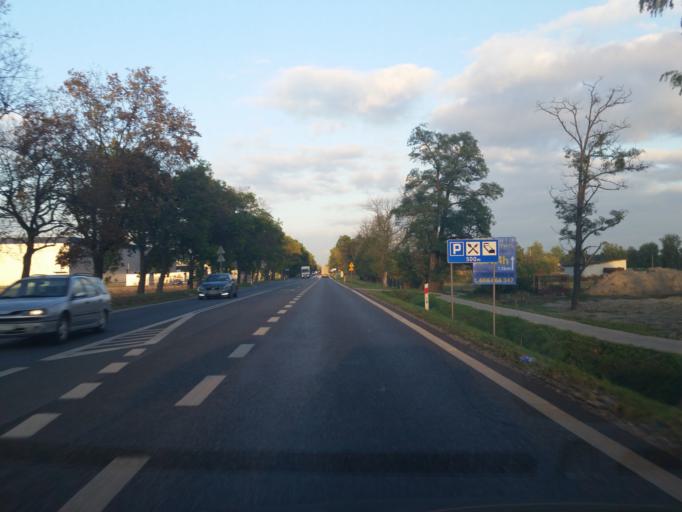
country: PL
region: Masovian Voivodeship
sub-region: Powiat warszawski zachodni
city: Jozefow
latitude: 52.2103
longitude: 20.6757
